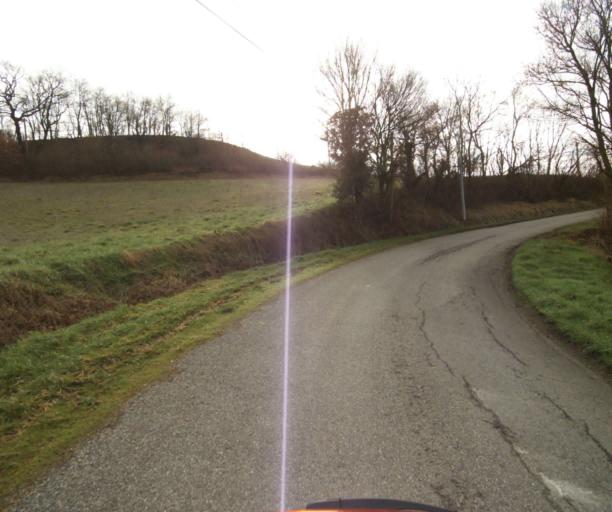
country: FR
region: Midi-Pyrenees
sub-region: Departement de la Haute-Garonne
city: Gaillac-Toulza
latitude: 43.1699
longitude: 1.5073
